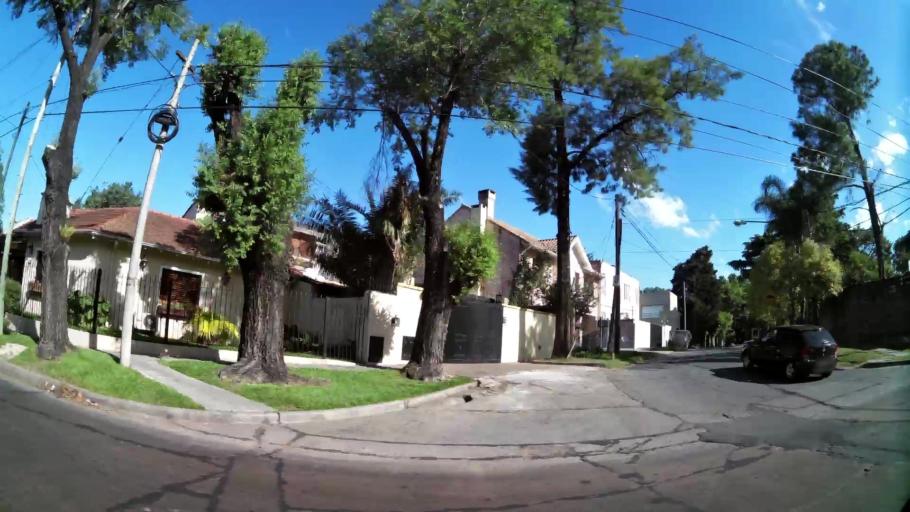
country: AR
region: Buenos Aires
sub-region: Partido de San Isidro
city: San Isidro
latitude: -34.4821
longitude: -58.5571
